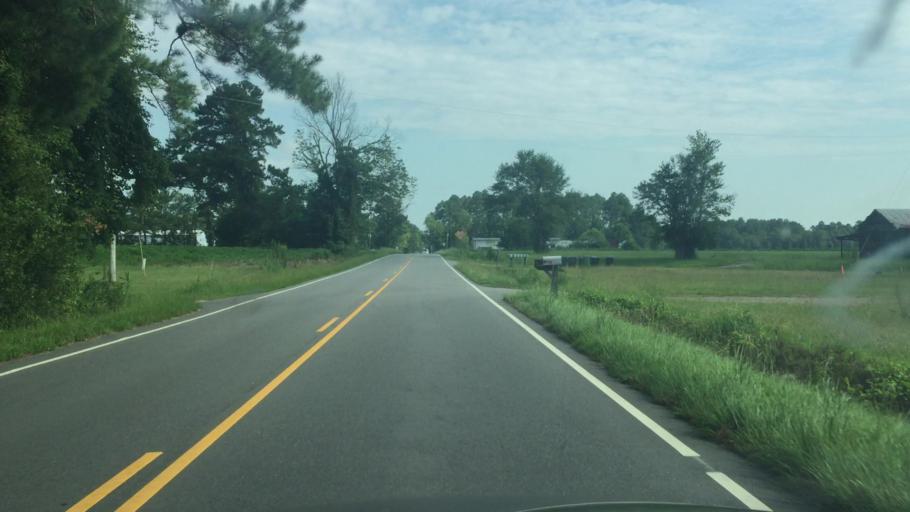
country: US
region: North Carolina
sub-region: Columbus County
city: Chadbourn
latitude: 34.3022
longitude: -78.8264
